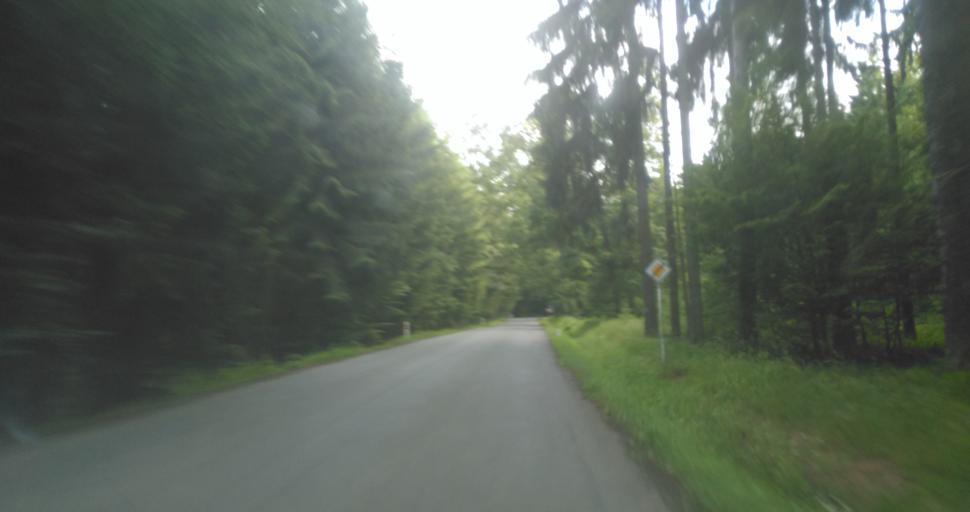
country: CZ
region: Central Bohemia
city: Hudlice
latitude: 49.9434
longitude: 13.9207
